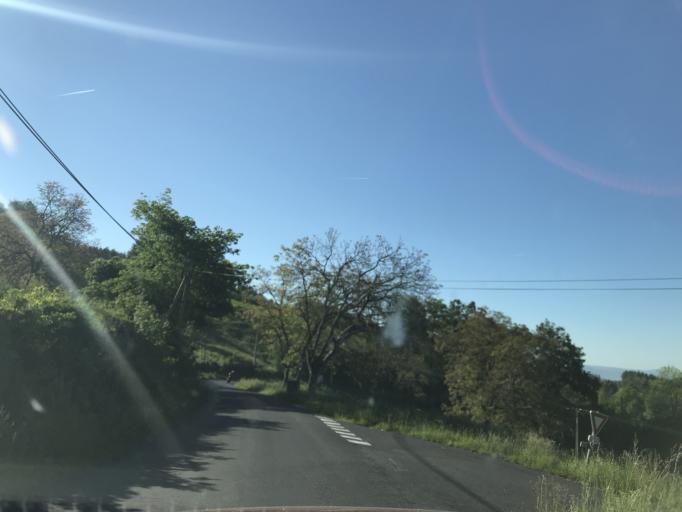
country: FR
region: Auvergne
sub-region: Departement du Puy-de-Dome
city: Job
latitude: 45.6748
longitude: 3.7005
